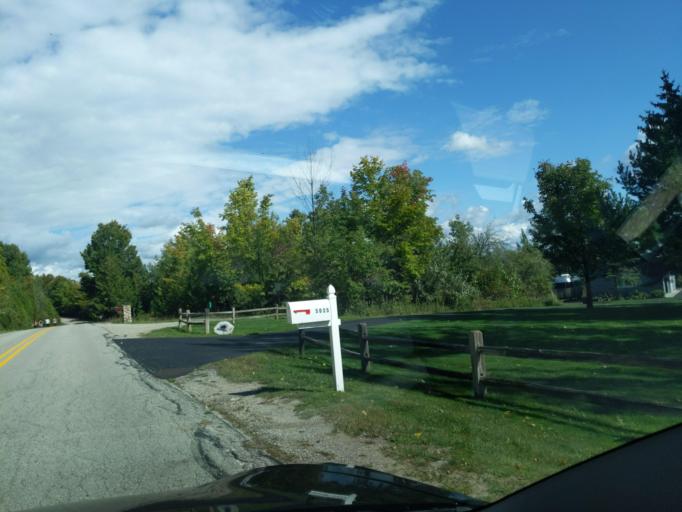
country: US
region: Michigan
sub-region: Antrim County
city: Elk Rapids
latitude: 44.9607
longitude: -85.3246
